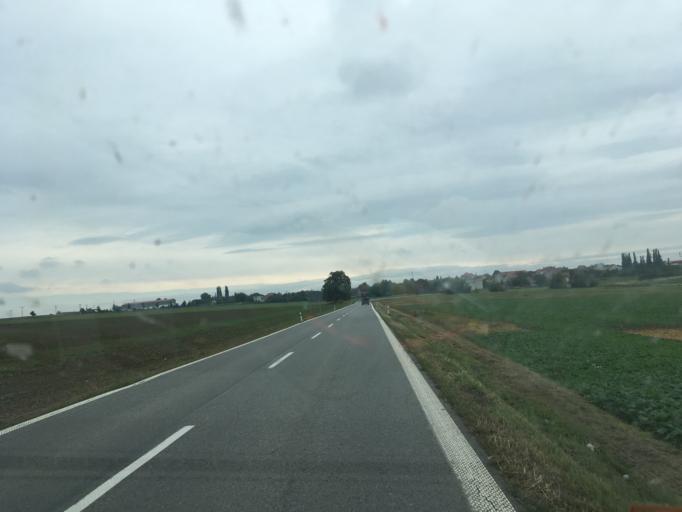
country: CZ
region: South Moravian
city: Zbraslav
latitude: 49.1927
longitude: 16.2439
